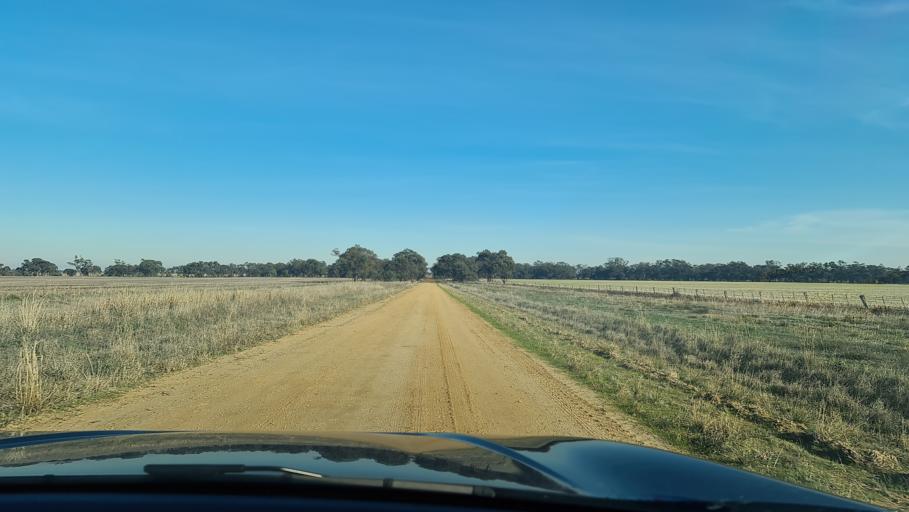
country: AU
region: Victoria
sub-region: Horsham
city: Horsham
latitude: -36.3538
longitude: 142.4032
